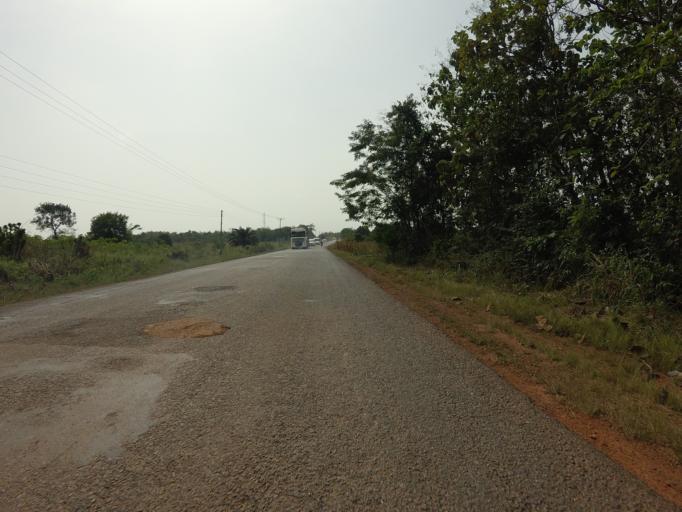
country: GH
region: Volta
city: Ho
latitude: 6.3834
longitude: 0.1858
